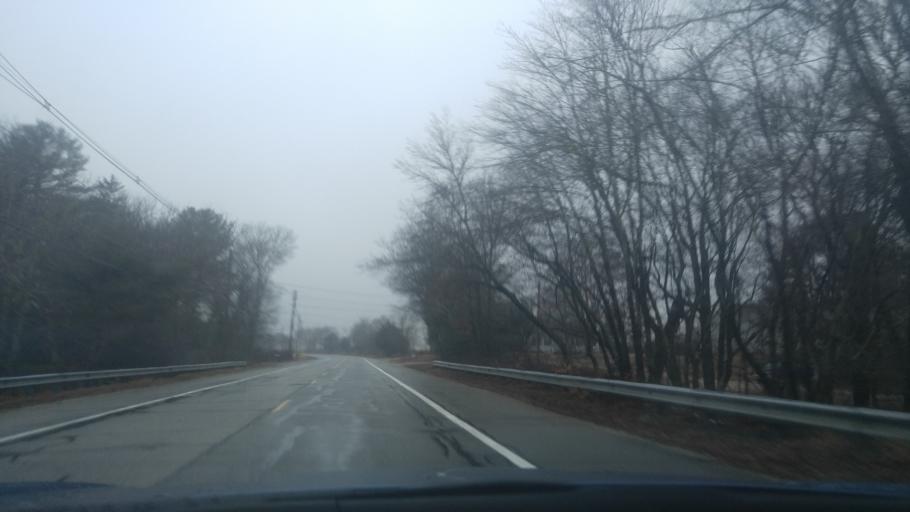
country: US
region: Rhode Island
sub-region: Washington County
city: Kingston
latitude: 41.4767
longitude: -71.6050
